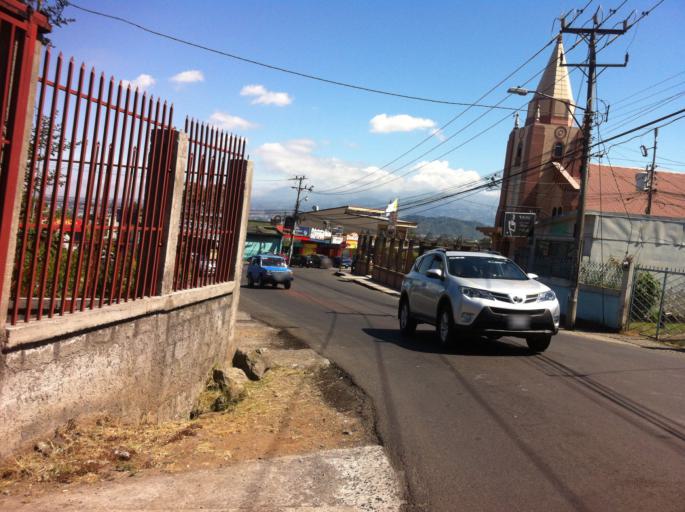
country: CR
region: San Jose
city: San Juan de Dios
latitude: 9.8785
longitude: -84.0840
